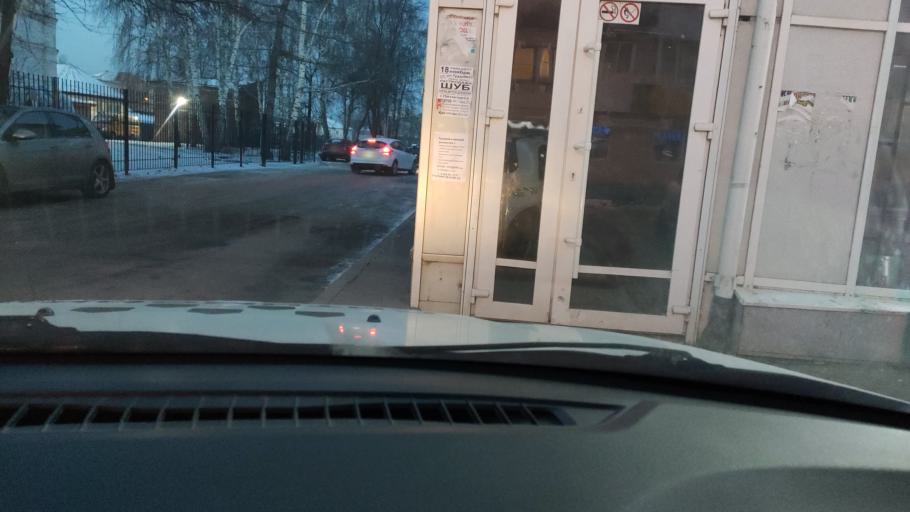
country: RU
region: Perm
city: Kungur
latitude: 57.4363
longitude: 56.9362
